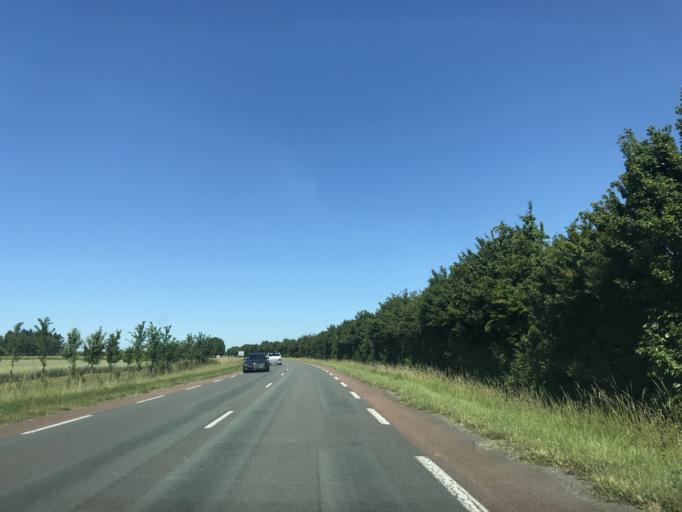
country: FR
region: Poitou-Charentes
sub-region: Departement de la Charente-Maritime
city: Gemozac
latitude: 45.5756
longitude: -0.6686
